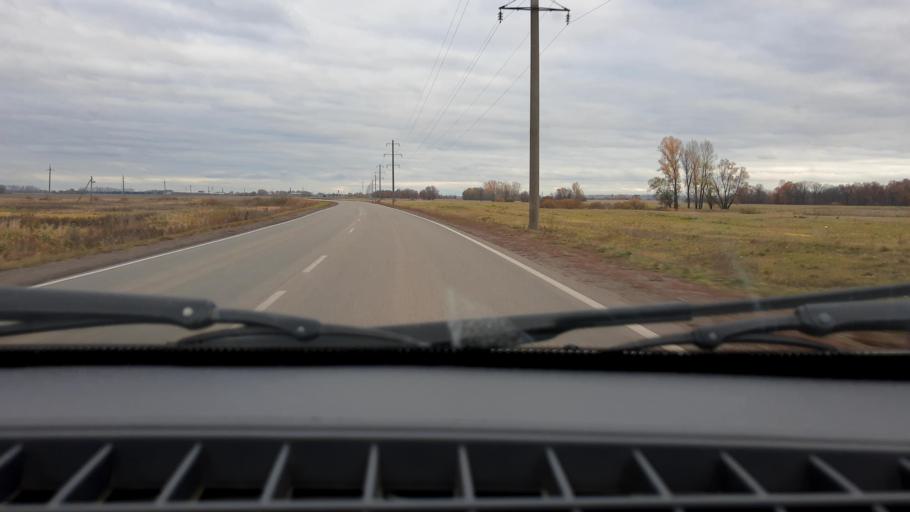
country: RU
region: Bashkortostan
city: Kabakovo
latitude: 54.5621
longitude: 55.9995
